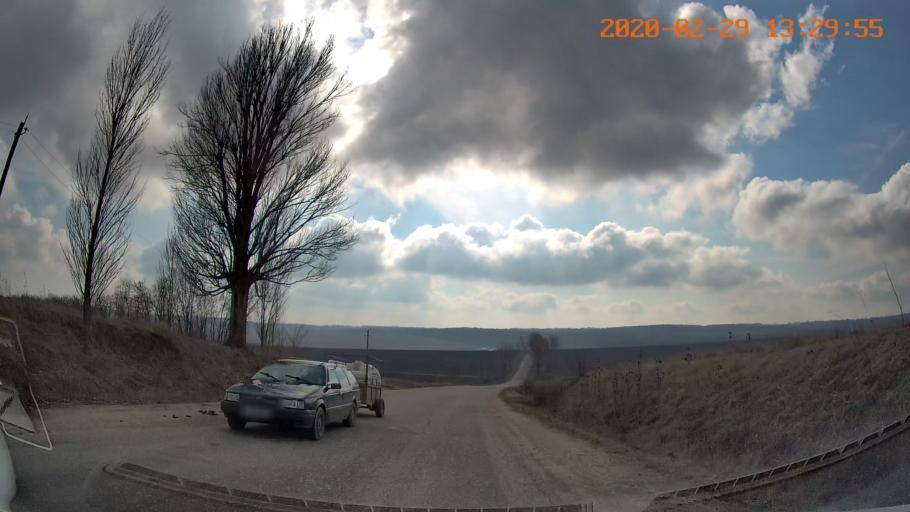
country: MD
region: Telenesti
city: Camenca
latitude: 47.8921
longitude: 28.6329
